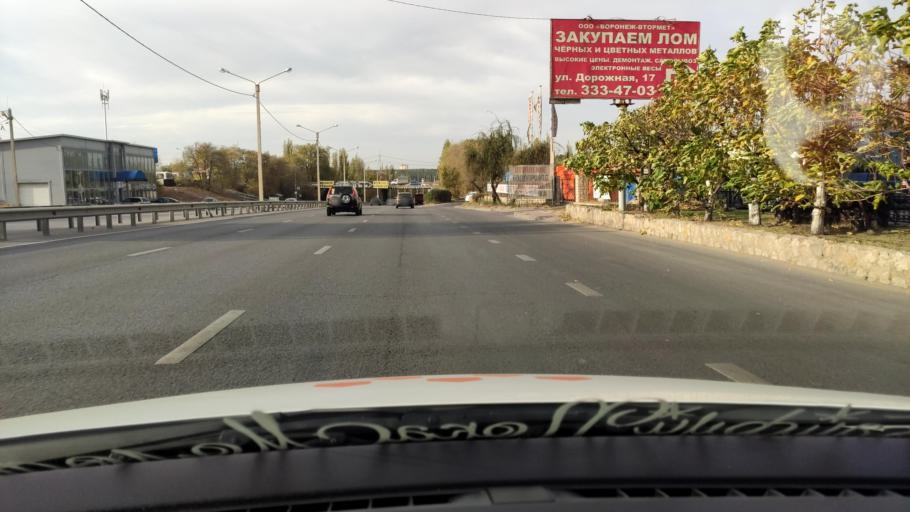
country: RU
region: Voronezj
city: Voronezh
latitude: 51.6597
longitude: 39.1325
